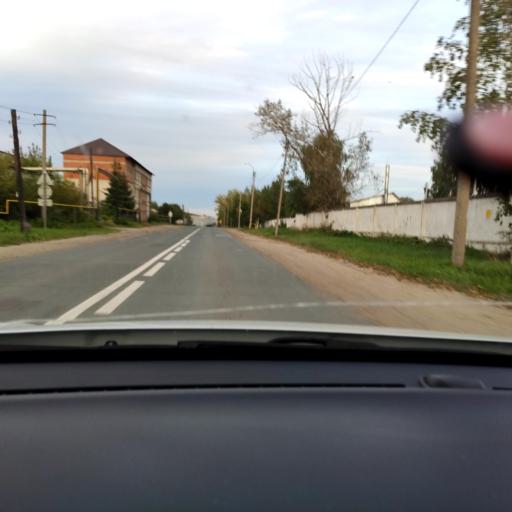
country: RU
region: Tatarstan
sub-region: Zelenodol'skiy Rayon
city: Zelenodolsk
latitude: 55.8384
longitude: 48.5351
